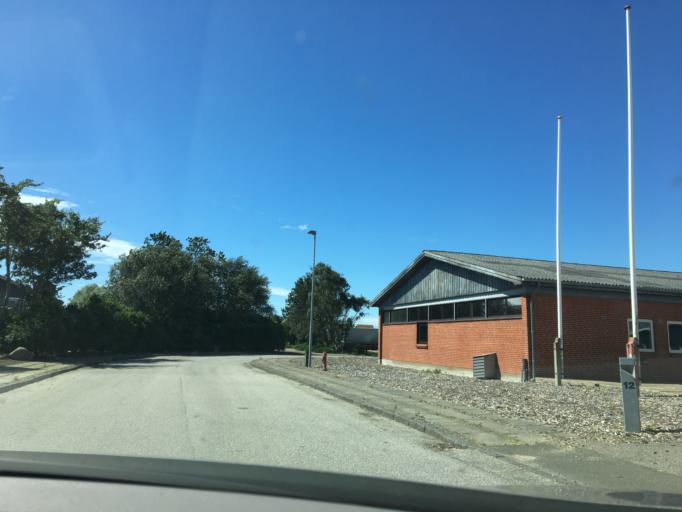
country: DK
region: Central Jutland
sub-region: Ringkobing-Skjern Kommune
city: Ringkobing
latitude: 56.0934
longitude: 8.2386
